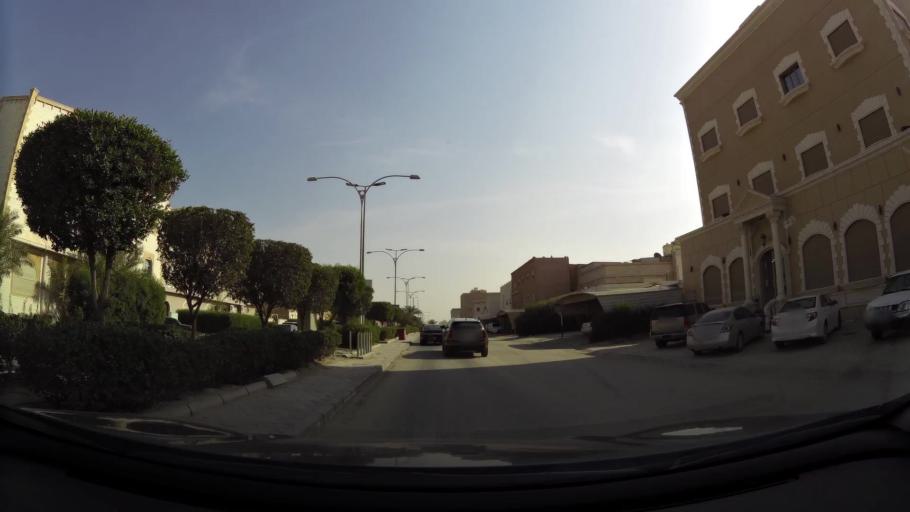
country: KW
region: Al Ahmadi
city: Ar Riqqah
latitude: 29.1519
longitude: 48.1049
